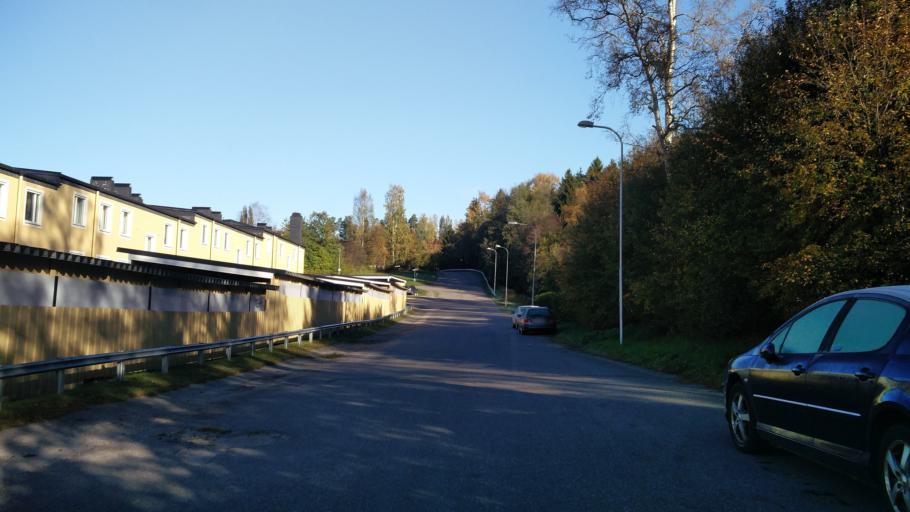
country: SE
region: Vaesternorrland
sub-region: Sundsvalls Kommun
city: Sundsvall
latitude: 62.4036
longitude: 17.2659
